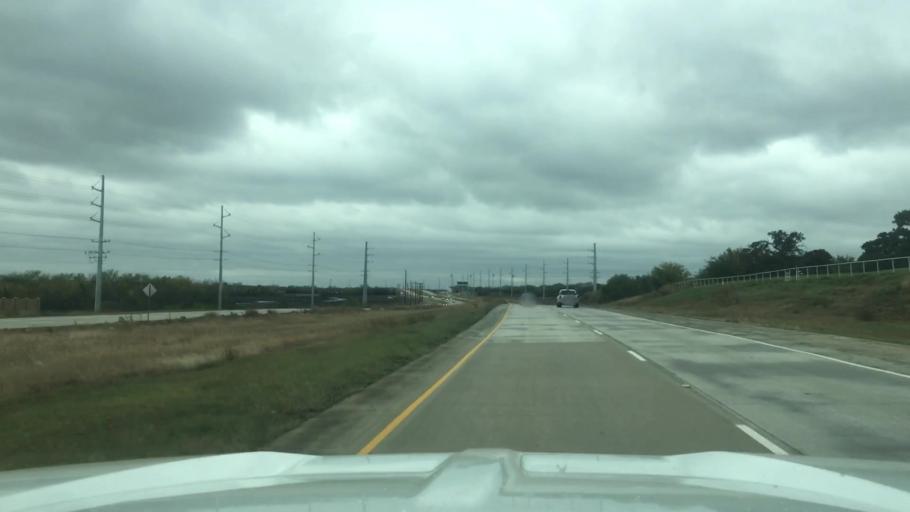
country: US
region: Texas
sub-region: Denton County
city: Denton
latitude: 33.2504
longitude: -97.0973
